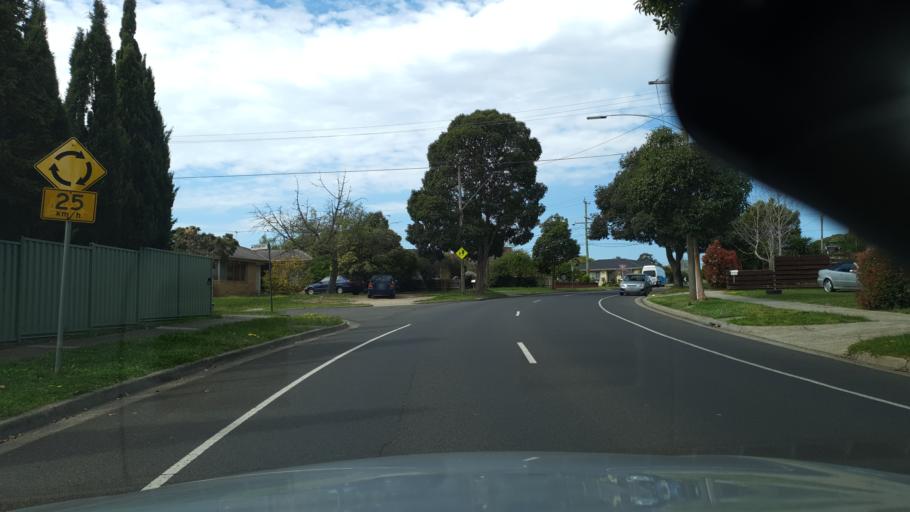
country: AU
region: Victoria
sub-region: Greater Dandenong
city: Springvale
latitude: -37.9233
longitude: 145.1679
